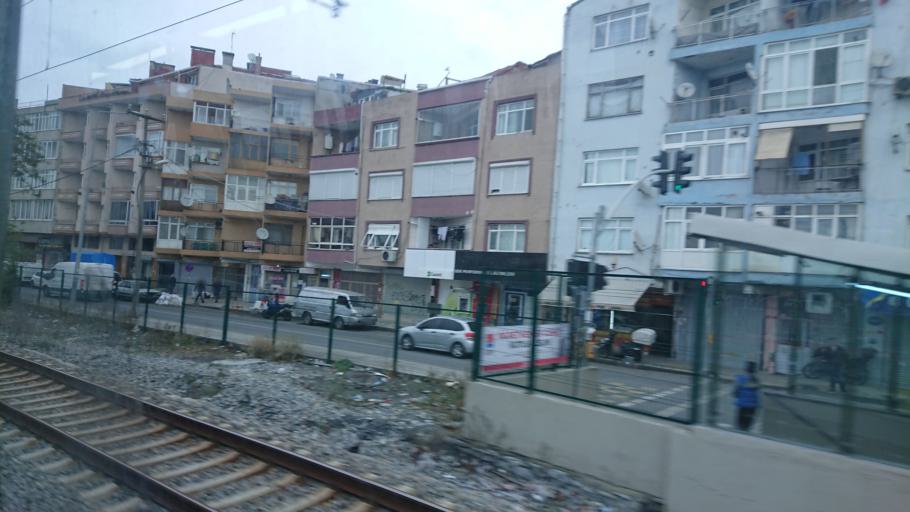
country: TR
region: Istanbul
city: Mahmutbey
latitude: 41.0102
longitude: 28.7739
